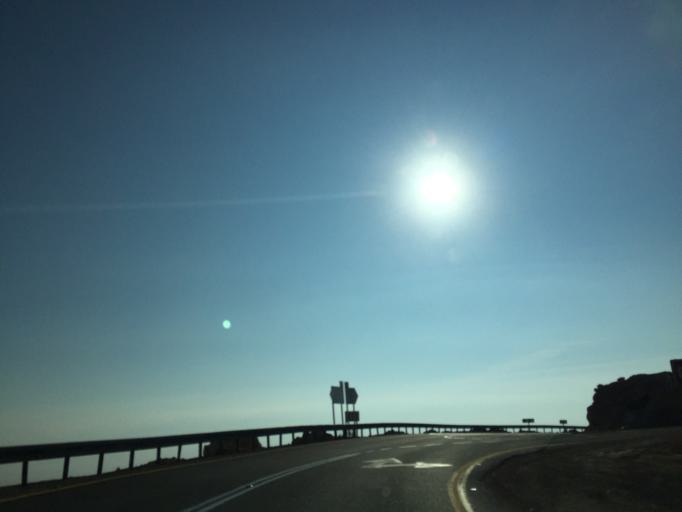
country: JO
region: Ma'an
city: Al Quwayrah
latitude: 30.0209
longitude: 35.0609
